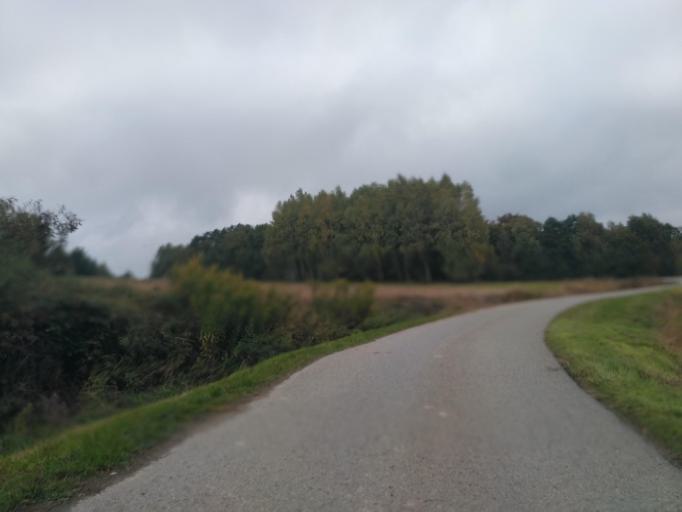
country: PL
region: Subcarpathian Voivodeship
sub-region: Powiat debicki
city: Brzostek
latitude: 49.9470
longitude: 21.4452
